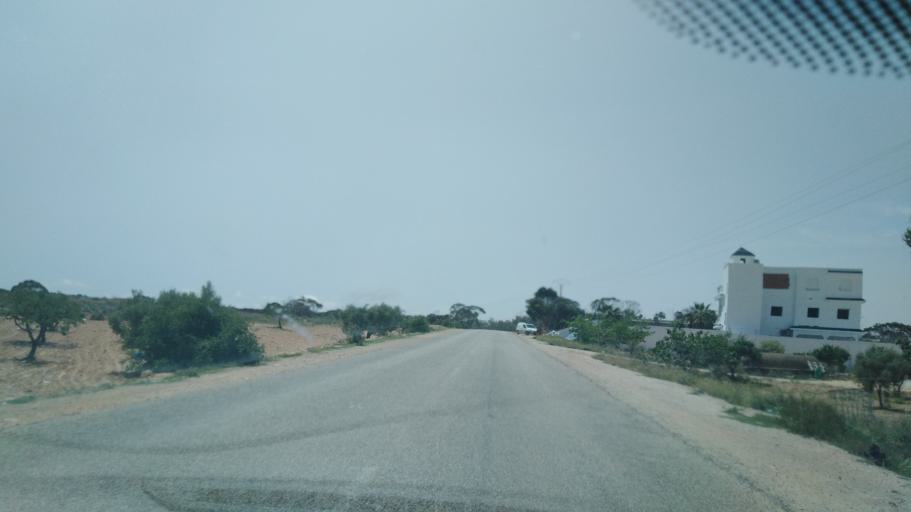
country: TN
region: Safaqis
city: Sfax
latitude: 34.7265
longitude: 10.5761
